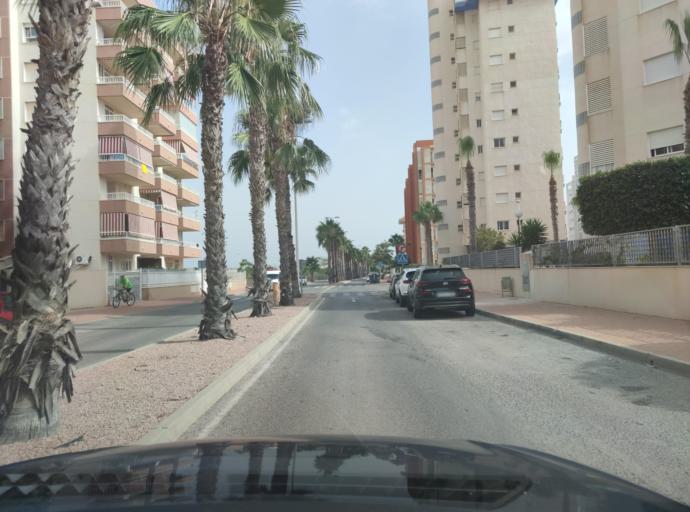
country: ES
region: Valencia
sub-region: Provincia de Alicante
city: Guardamar del Segura
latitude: 38.1010
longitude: -0.6557
